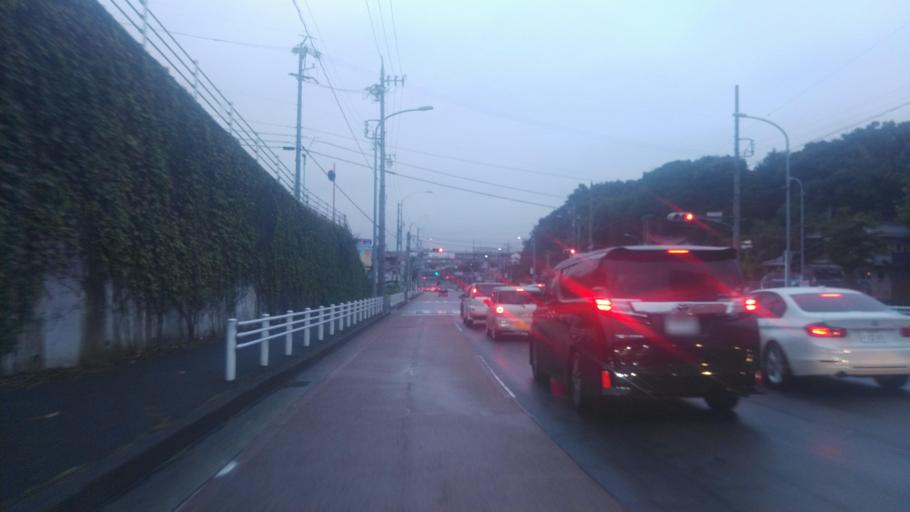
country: JP
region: Aichi
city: Kasugai
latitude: 35.2220
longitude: 136.9861
